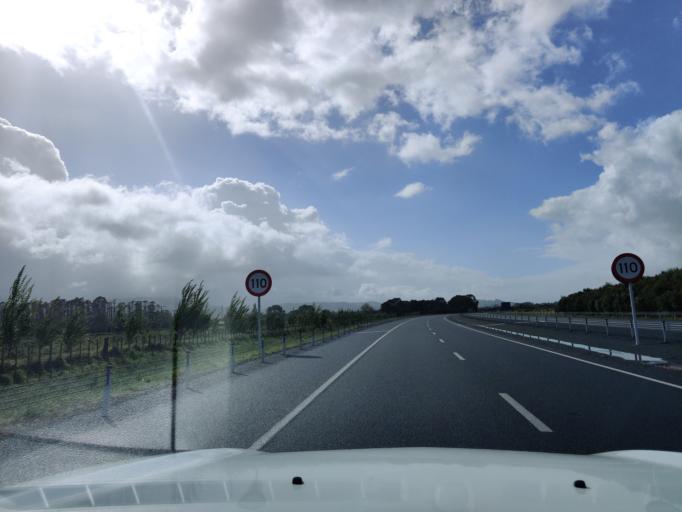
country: NZ
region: Waikato
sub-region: Waipa District
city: Cambridge
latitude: -37.8695
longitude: 175.4730
